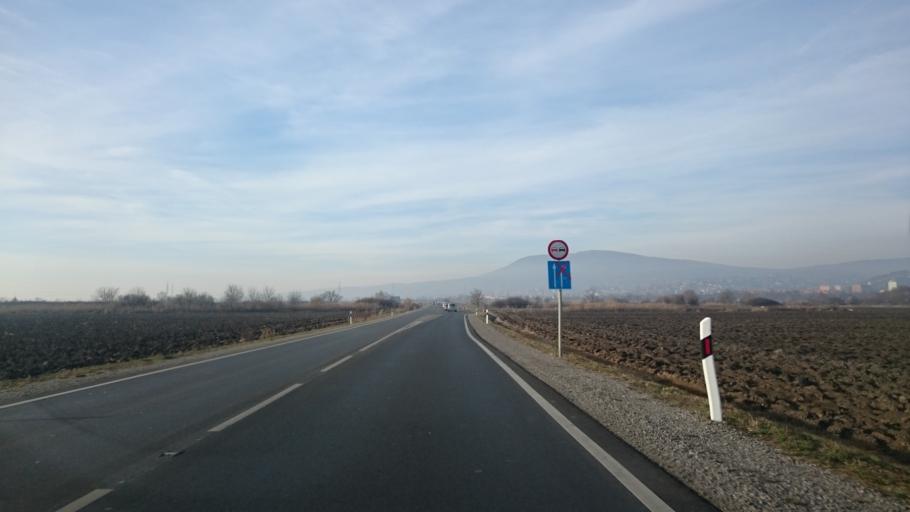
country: HU
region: Baranya
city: Pecs
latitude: 46.0496
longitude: 18.2036
